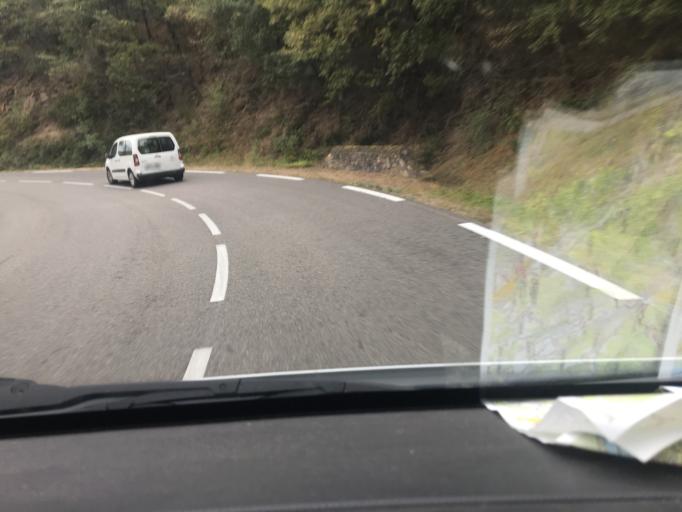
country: FR
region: Rhone-Alpes
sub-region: Departement de l'Ardeche
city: Saint-Jean-de-Muzols
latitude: 45.0648
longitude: 4.7507
